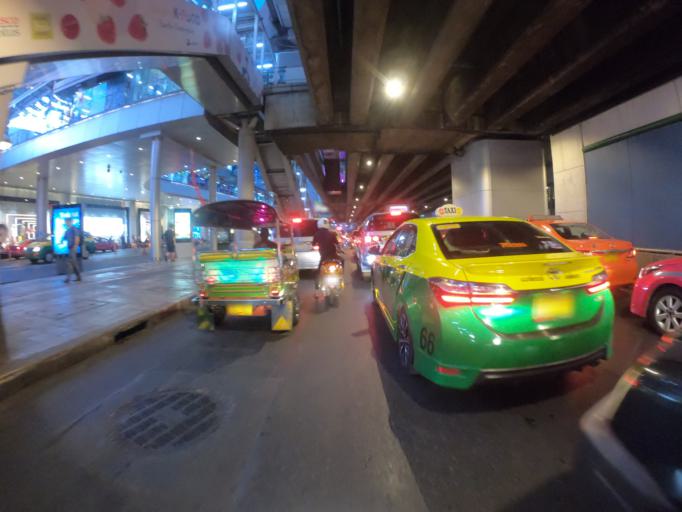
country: TH
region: Bangkok
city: Khlong Toei
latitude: 13.7375
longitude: 100.5599
